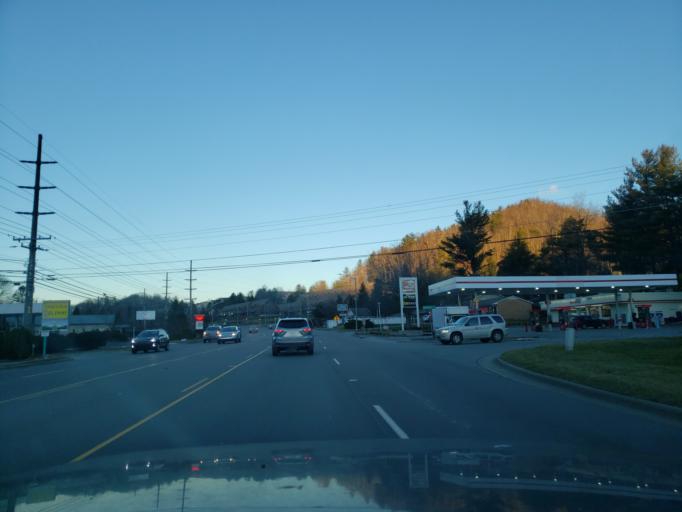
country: US
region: North Carolina
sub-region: Watauga County
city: Boone
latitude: 36.2063
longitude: -81.6980
